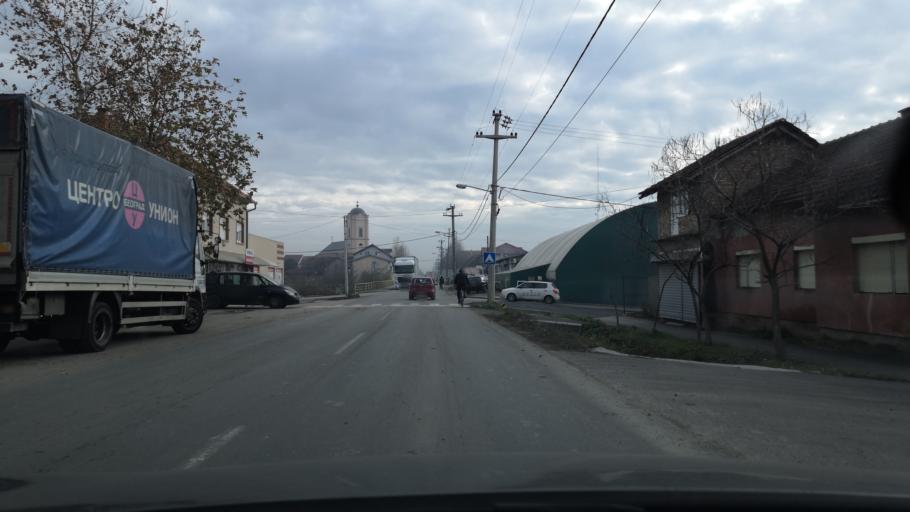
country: RS
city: Ugrinovci
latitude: 44.8766
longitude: 20.1844
